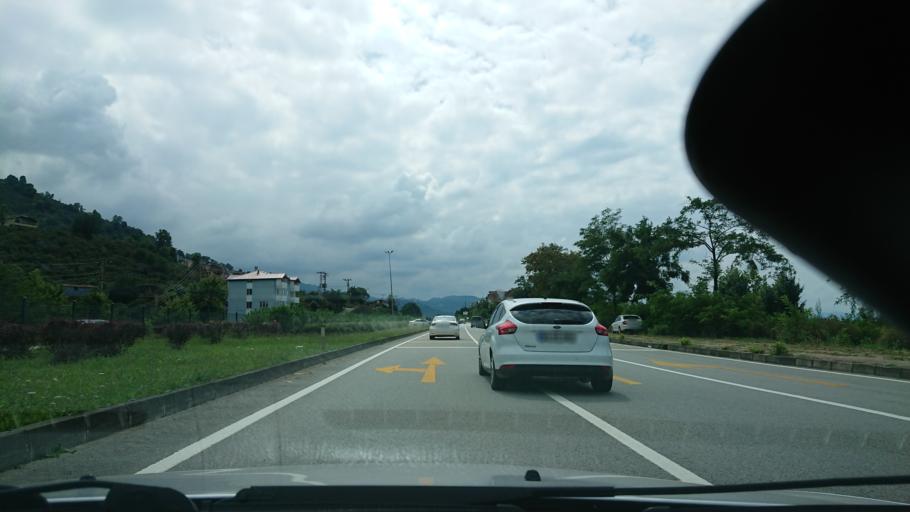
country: TR
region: Giresun
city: Kesap
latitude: 40.9293
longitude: 38.5602
